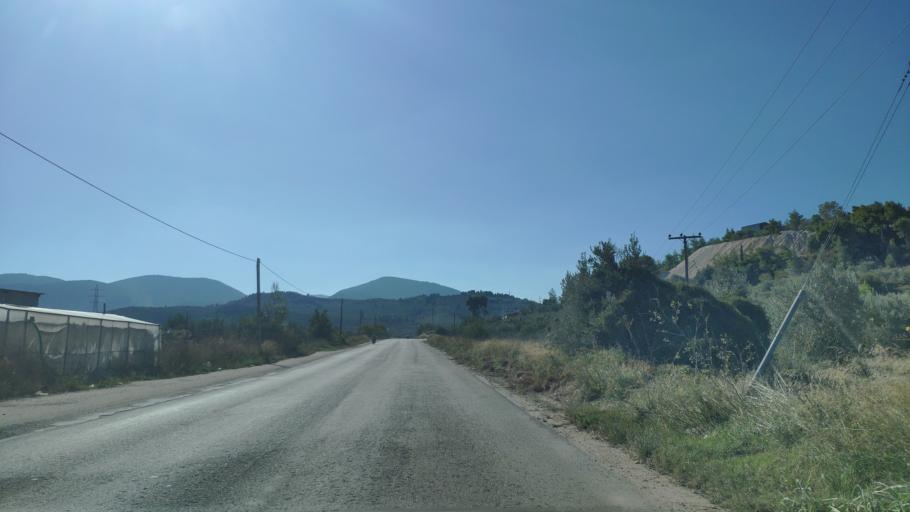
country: GR
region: Peloponnese
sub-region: Nomos Korinthias
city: Athikia
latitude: 37.8430
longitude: 22.8993
